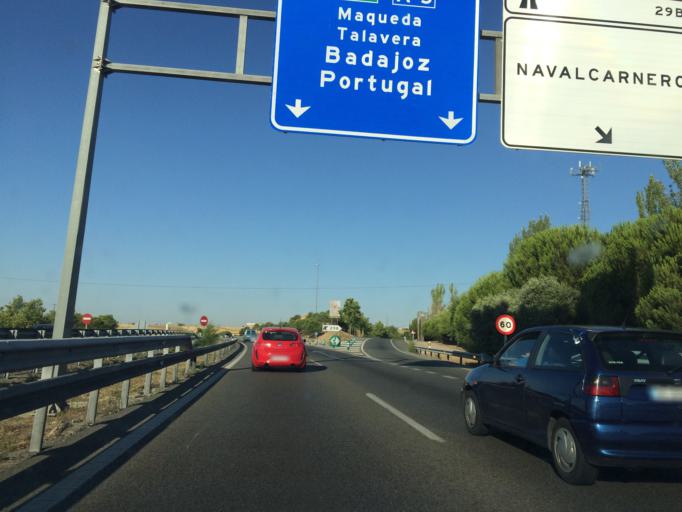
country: ES
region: Madrid
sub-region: Provincia de Madrid
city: Navalcarnero
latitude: 40.2903
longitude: -3.9911
